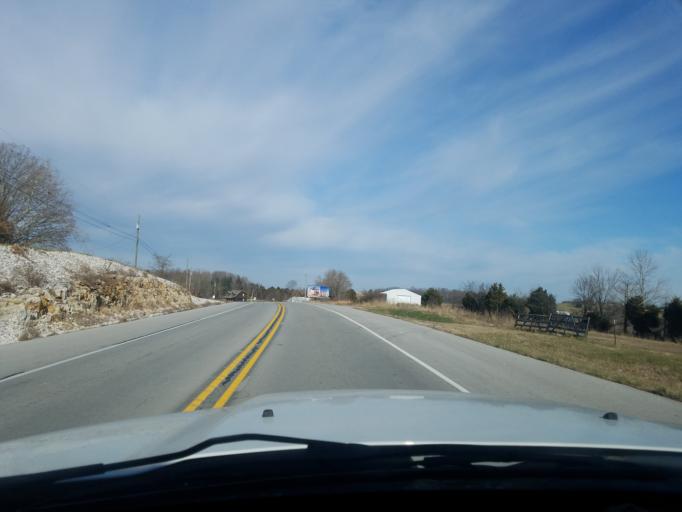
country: US
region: Indiana
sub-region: Orange County
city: Paoli
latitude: 38.5870
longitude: -86.4540
